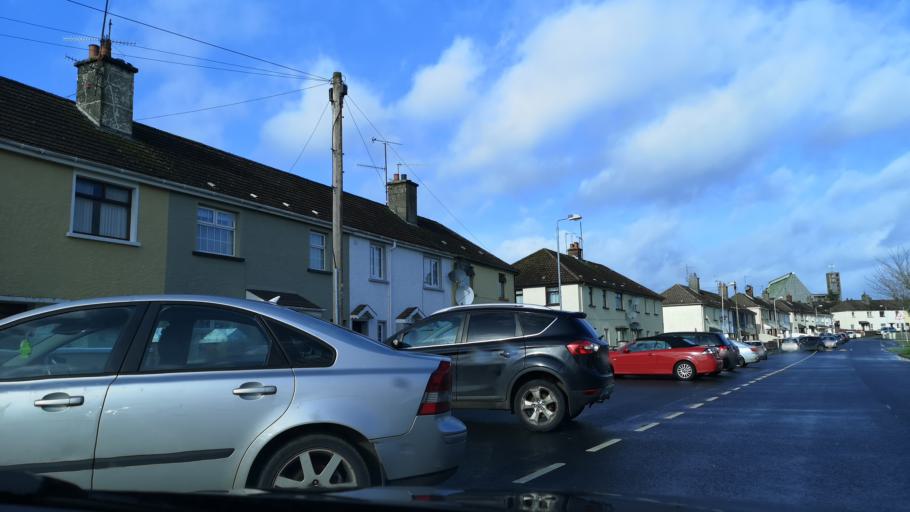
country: GB
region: Northern Ireland
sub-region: Newry and Mourne District
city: Newry
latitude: 54.1826
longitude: -6.3492
